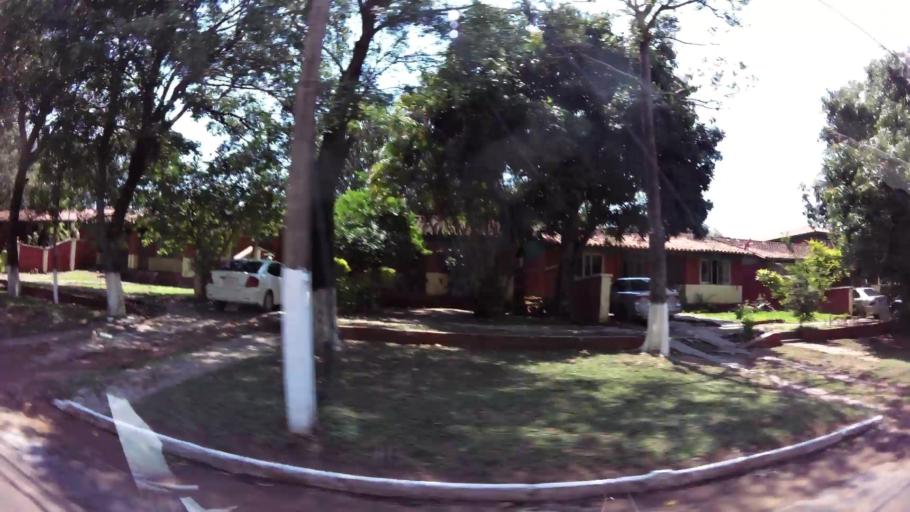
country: PY
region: Asuncion
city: Asuncion
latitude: -25.3025
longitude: -57.6564
